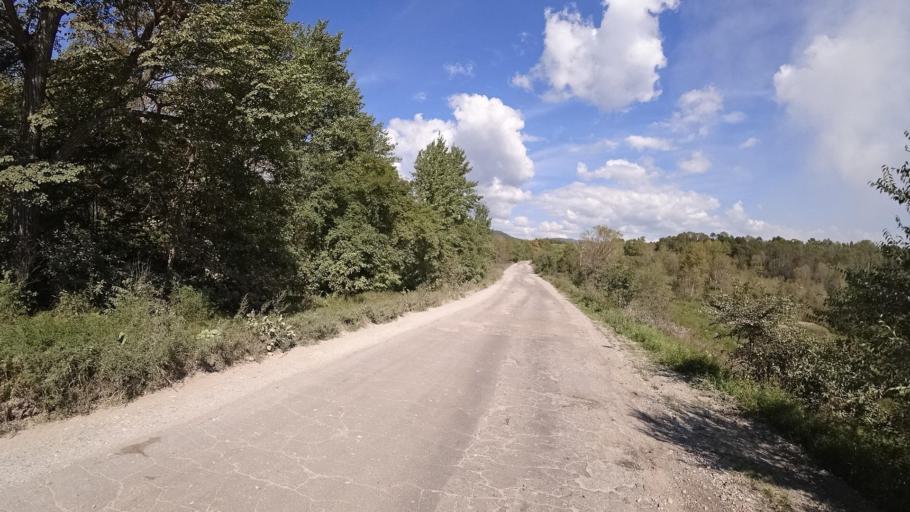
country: RU
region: Jewish Autonomous Oblast
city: Londoko
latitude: 49.0081
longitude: 131.8942
